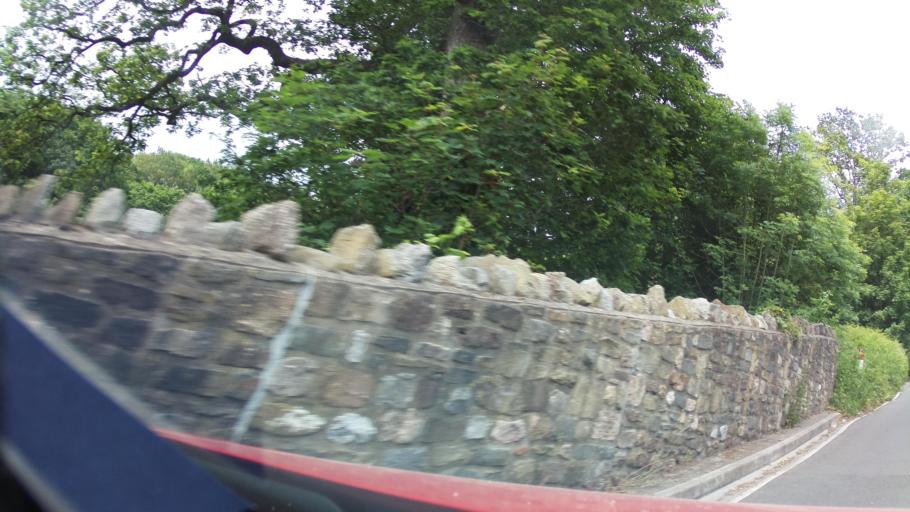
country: GB
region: England
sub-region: South Gloucestershire
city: Kingswood
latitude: 51.4463
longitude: -2.5340
